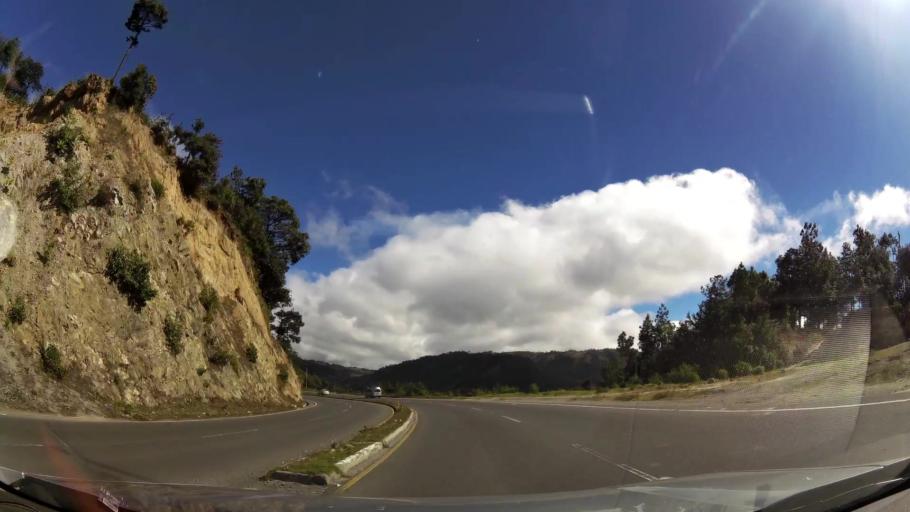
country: GT
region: Solola
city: Solola
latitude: 14.8276
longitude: -91.1843
